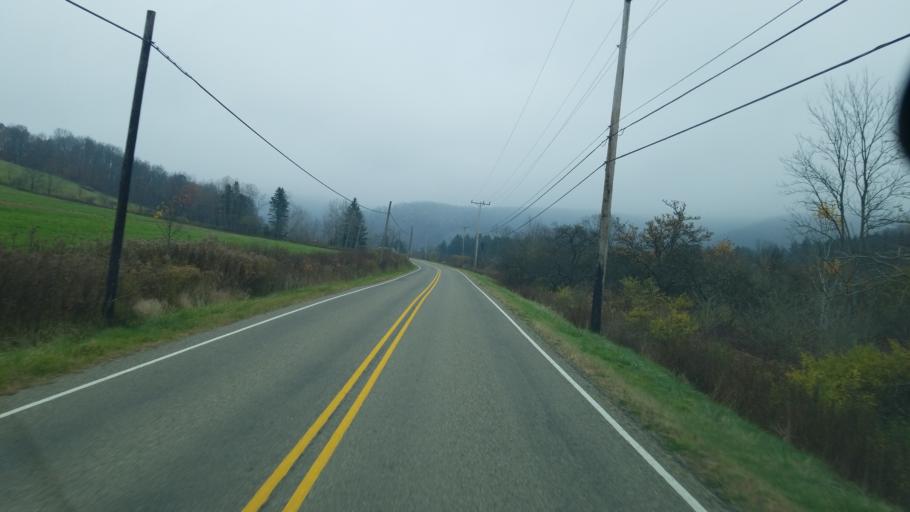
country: US
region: Pennsylvania
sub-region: McKean County
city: Smethport
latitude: 41.8660
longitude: -78.4751
